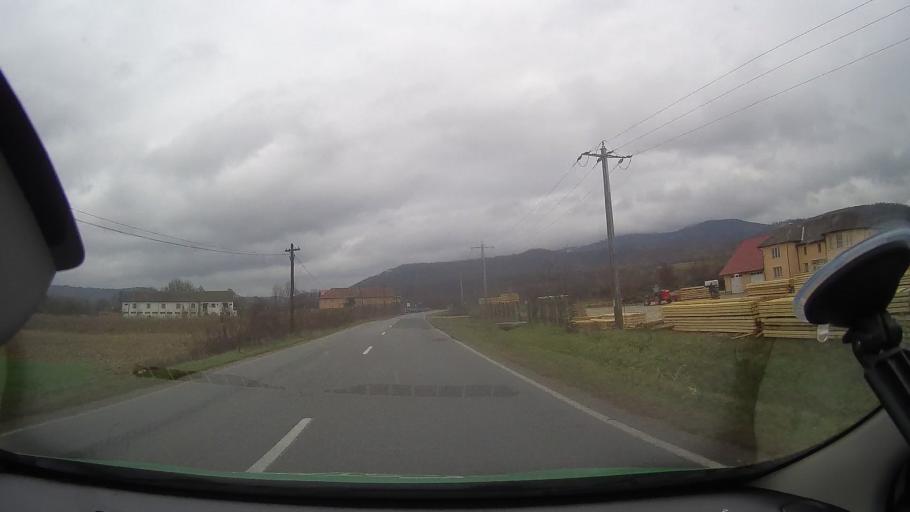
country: RO
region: Arad
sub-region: Comuna Buteni
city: Buteni
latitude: 46.3122
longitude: 22.1424
